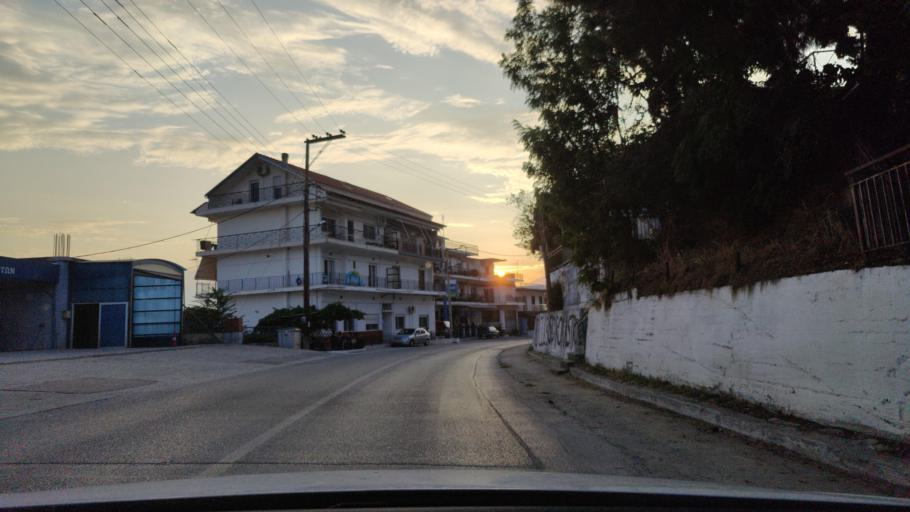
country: GR
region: Central Macedonia
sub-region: Nomos Serron
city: Sidirokastro
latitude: 41.2399
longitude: 23.3891
